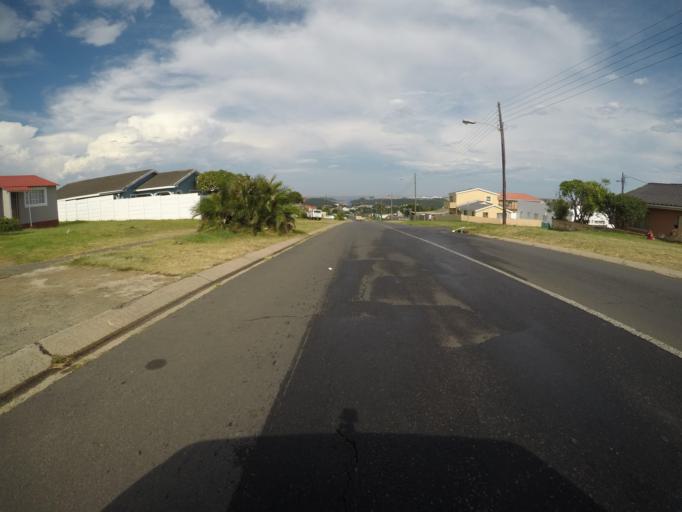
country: ZA
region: Eastern Cape
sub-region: Buffalo City Metropolitan Municipality
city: East London
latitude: -33.0224
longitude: 27.8736
